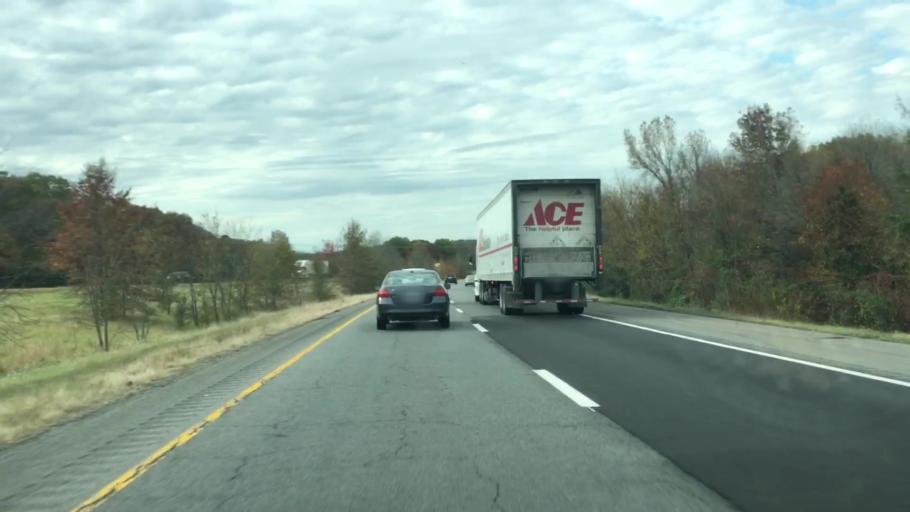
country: US
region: Arkansas
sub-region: Faulkner County
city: Conway
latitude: 35.1242
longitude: -92.5066
